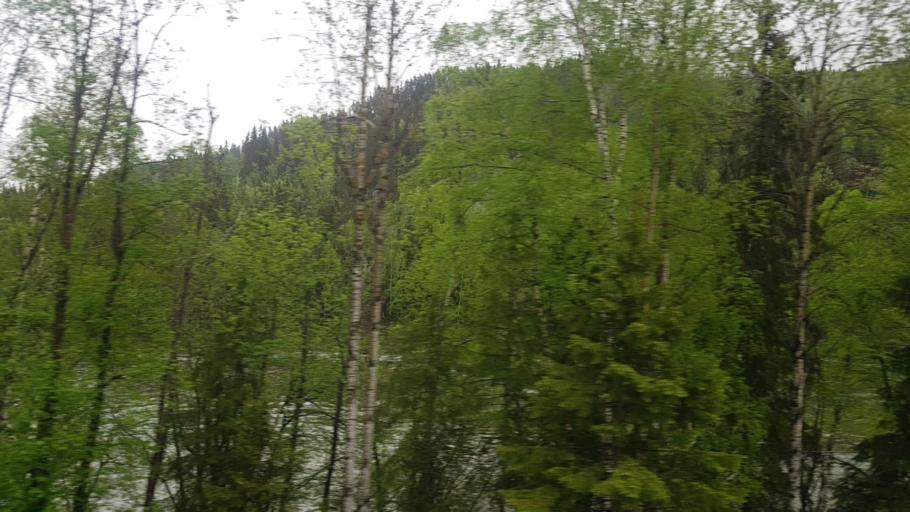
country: NO
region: Oppland
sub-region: Oyer
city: Tretten
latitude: 61.3218
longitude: 10.2931
